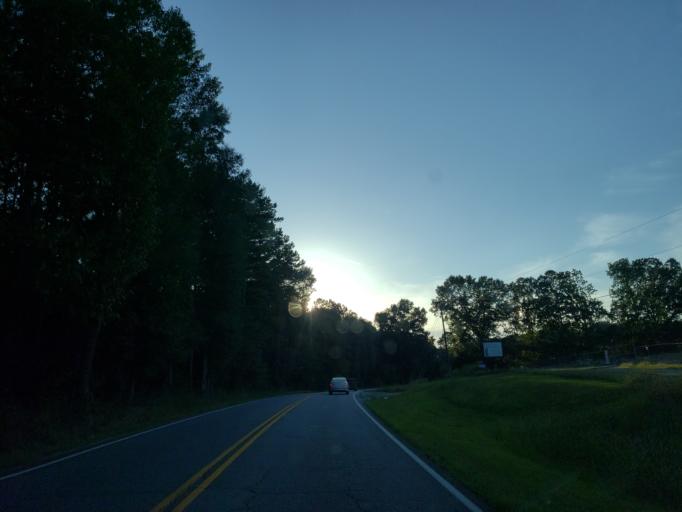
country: US
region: Georgia
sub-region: Bartow County
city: Euharlee
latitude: 34.2380
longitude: -84.9918
